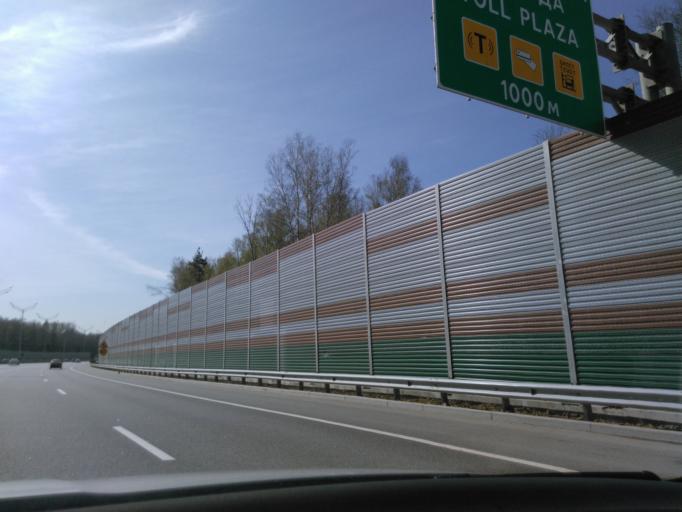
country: RU
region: Moscow
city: Khimki
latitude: 55.9441
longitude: 37.4455
